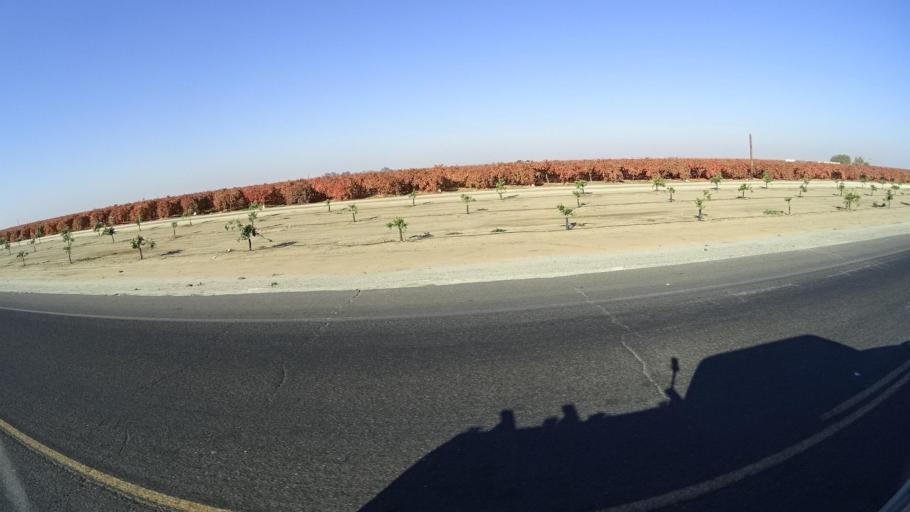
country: US
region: California
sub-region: Tulare County
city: Richgrove
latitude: 35.7387
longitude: -119.1468
